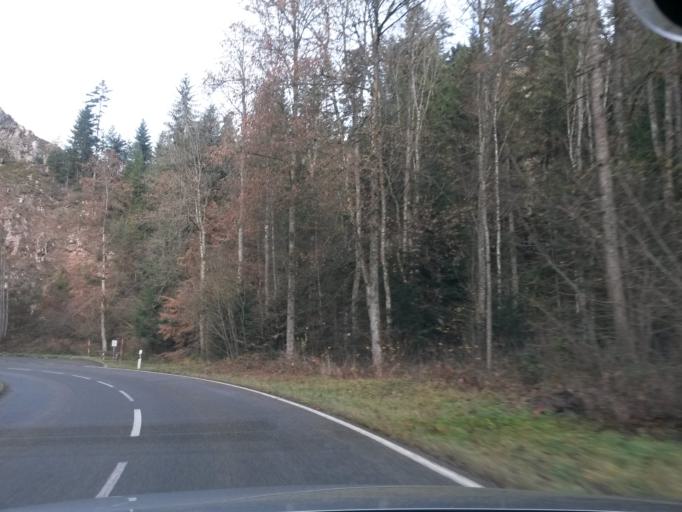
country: DE
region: Baden-Wuerttemberg
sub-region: Freiburg Region
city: Schramberg
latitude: 48.1944
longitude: 8.3847
